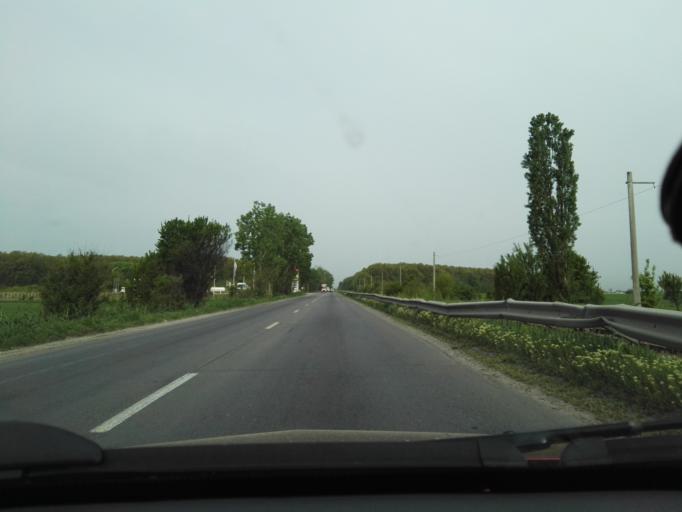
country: RO
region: Ilfov
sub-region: Comuna Magurele
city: Alunisu
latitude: 44.3504
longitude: 26.0636
